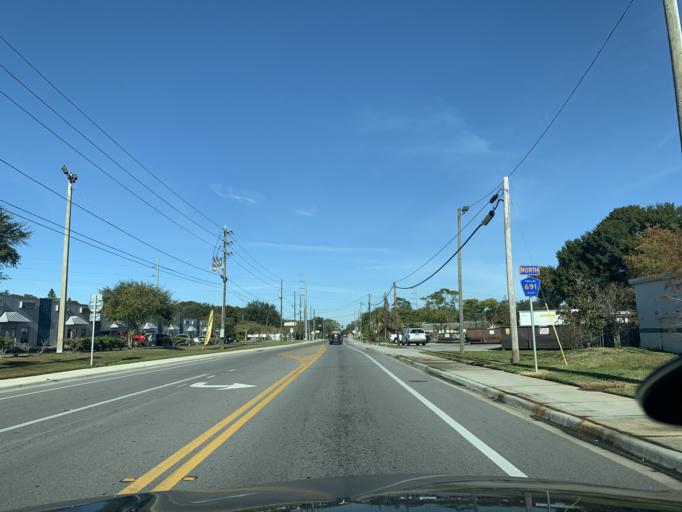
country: US
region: Florida
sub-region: Pinellas County
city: Lealman
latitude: 27.8221
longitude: -82.6696
